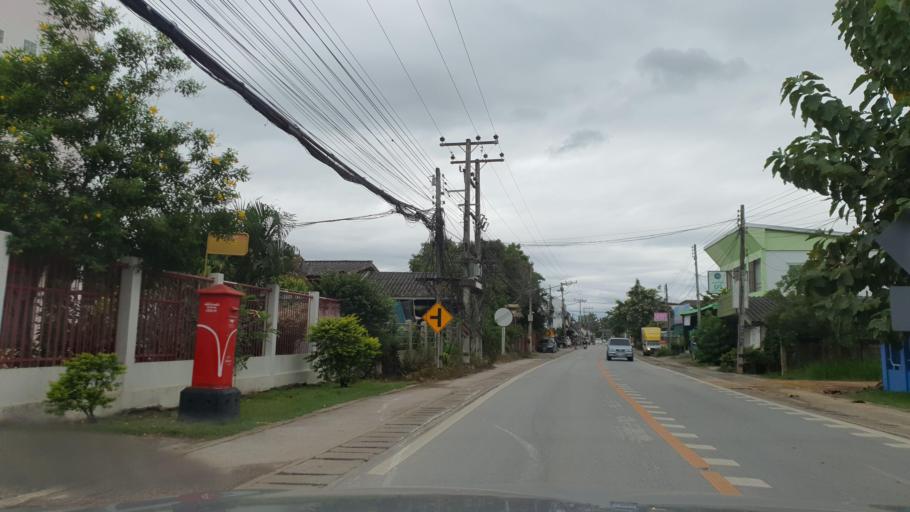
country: TH
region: Chiang Mai
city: San Pa Tong
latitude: 18.6177
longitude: 98.9484
